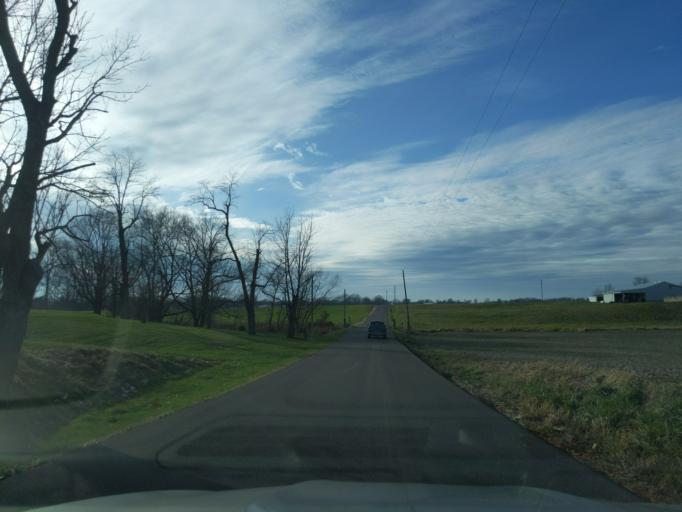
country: US
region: Indiana
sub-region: Decatur County
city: Westport
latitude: 39.1835
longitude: -85.5586
